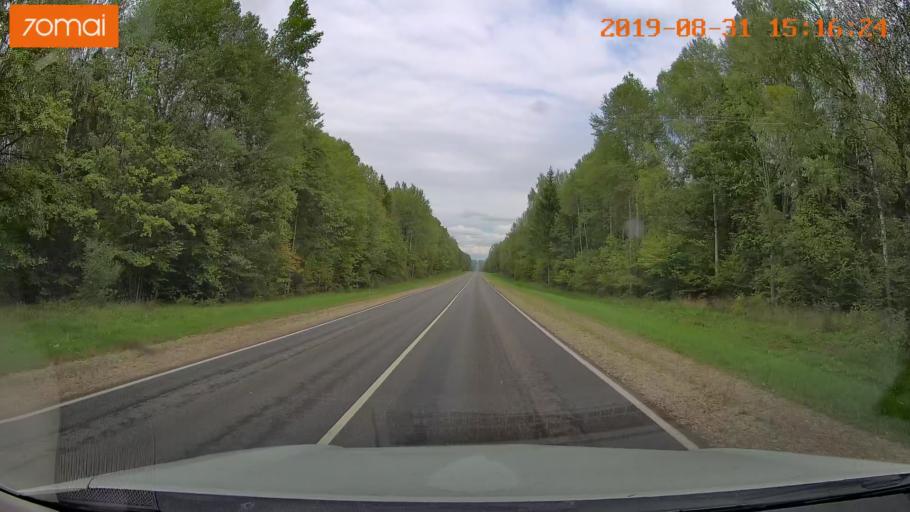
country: RU
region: Kaluga
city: Baryatino
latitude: 54.4596
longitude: 34.3493
